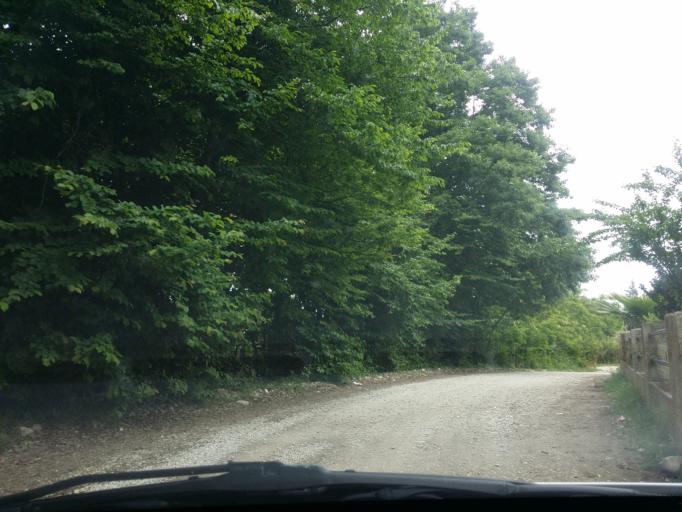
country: IR
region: Mazandaran
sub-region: Nowshahr
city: Nowshahr
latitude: 36.6203
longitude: 51.4937
